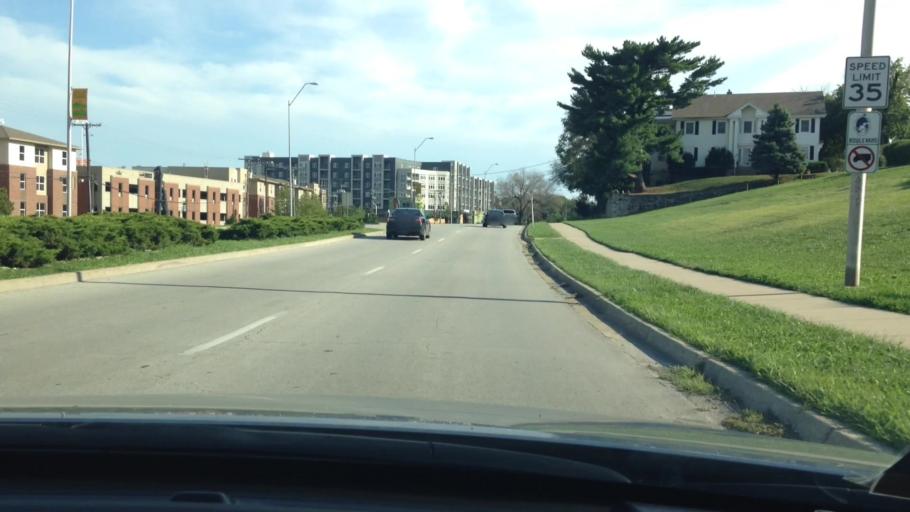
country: US
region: Kansas
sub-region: Johnson County
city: Westwood
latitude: 39.0374
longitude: -94.5846
